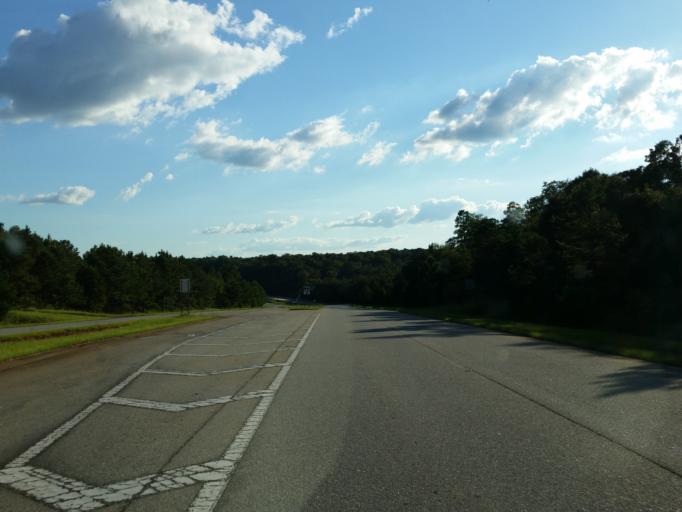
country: US
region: Georgia
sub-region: Houston County
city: Perry
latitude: 32.4793
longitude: -83.7739
